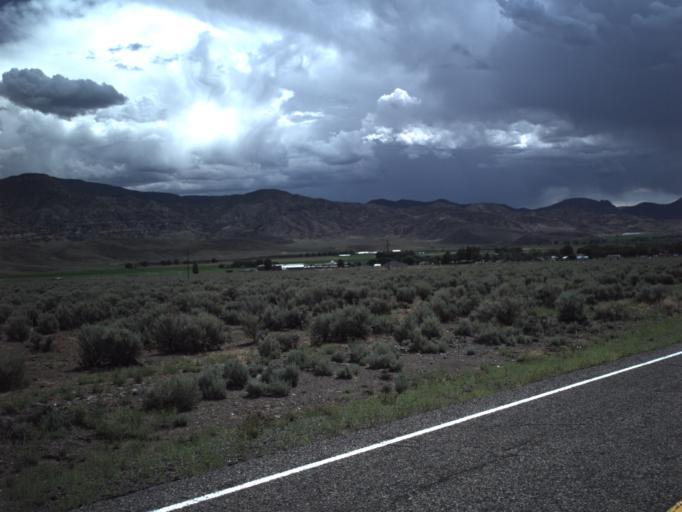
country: US
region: Utah
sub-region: Piute County
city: Junction
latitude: 38.2482
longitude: -112.2369
